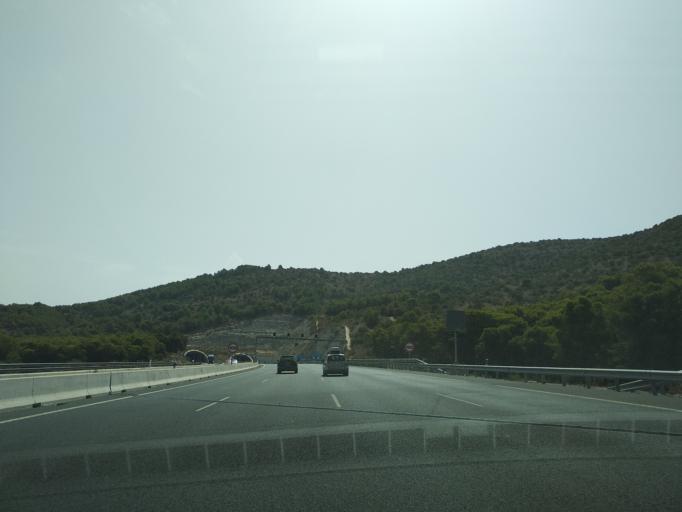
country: ES
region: Andalusia
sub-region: Provincia de Malaga
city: Alhaurin de la Torre
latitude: 36.6601
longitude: -4.5254
